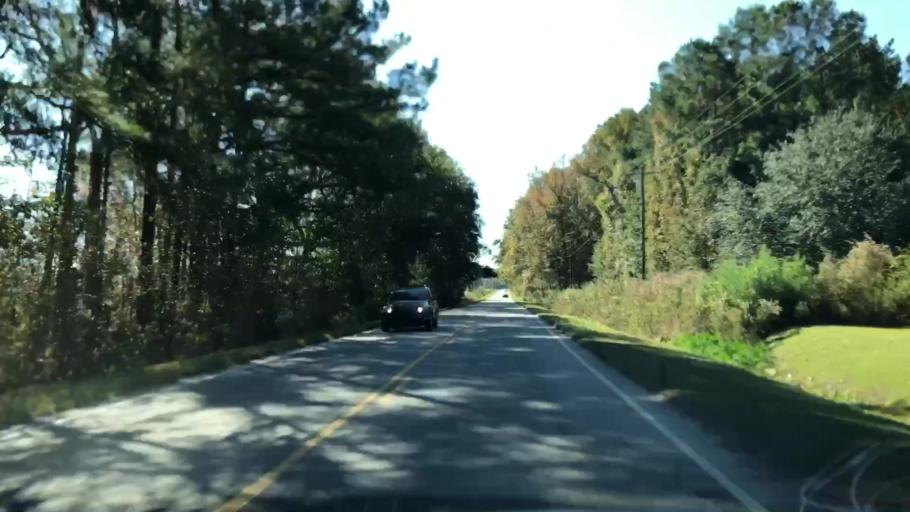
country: US
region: South Carolina
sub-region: Jasper County
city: Ridgeland
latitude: 32.4274
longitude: -80.8966
